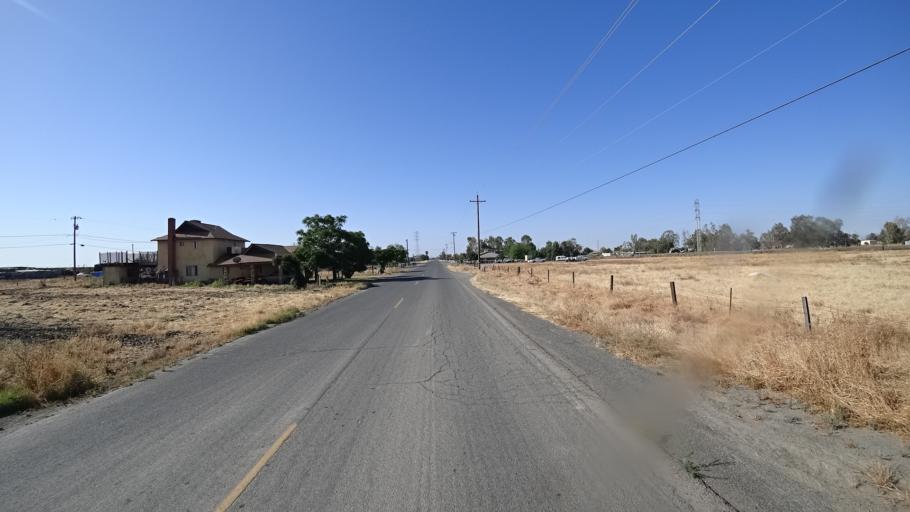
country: US
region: California
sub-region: Kings County
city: Corcoran
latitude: 36.1231
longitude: -119.5634
